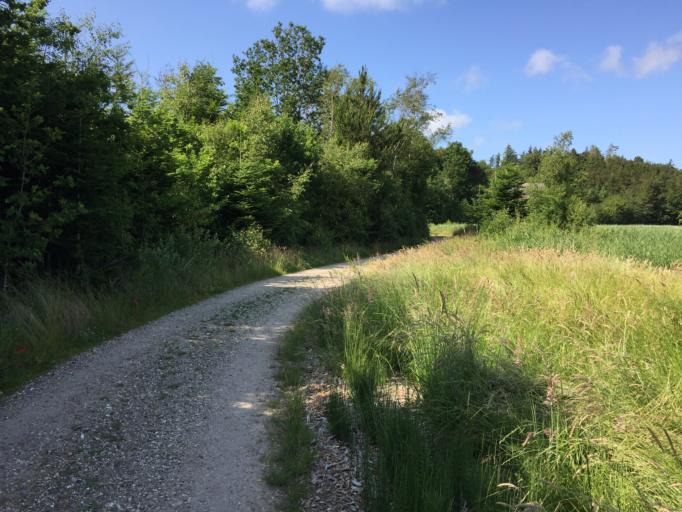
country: DK
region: North Denmark
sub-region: Thisted Kommune
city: Hurup
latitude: 56.6853
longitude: 8.4080
